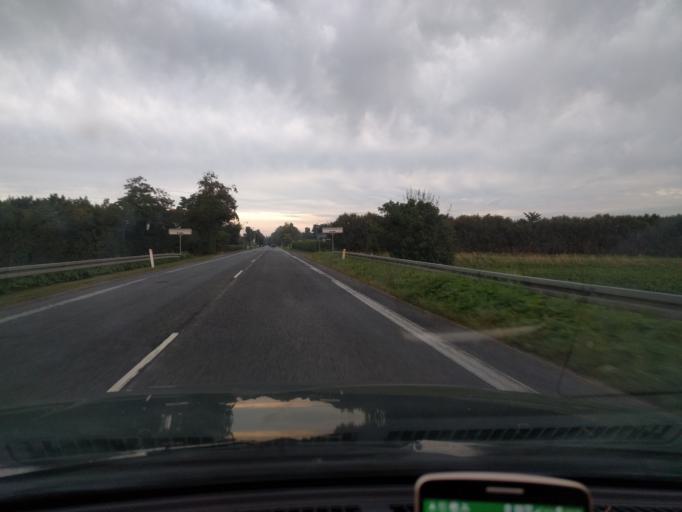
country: DK
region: Zealand
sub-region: Guldborgsund Kommune
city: Stubbekobing
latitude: 54.8905
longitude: 12.0178
